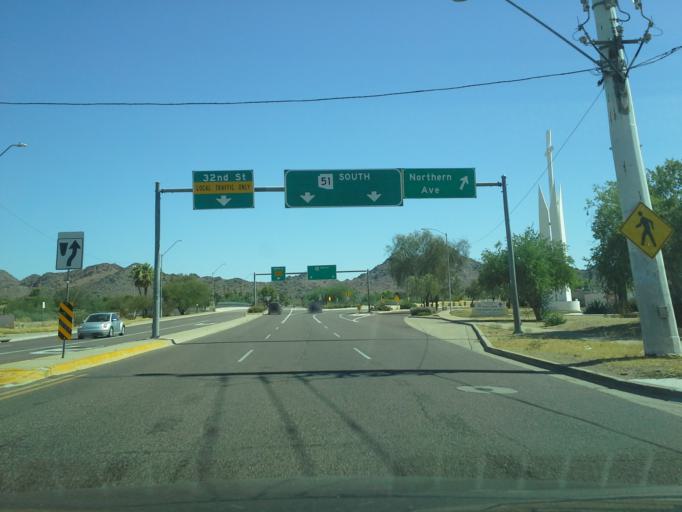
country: US
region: Arizona
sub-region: Maricopa County
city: Paradise Valley
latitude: 33.5789
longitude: -112.0132
